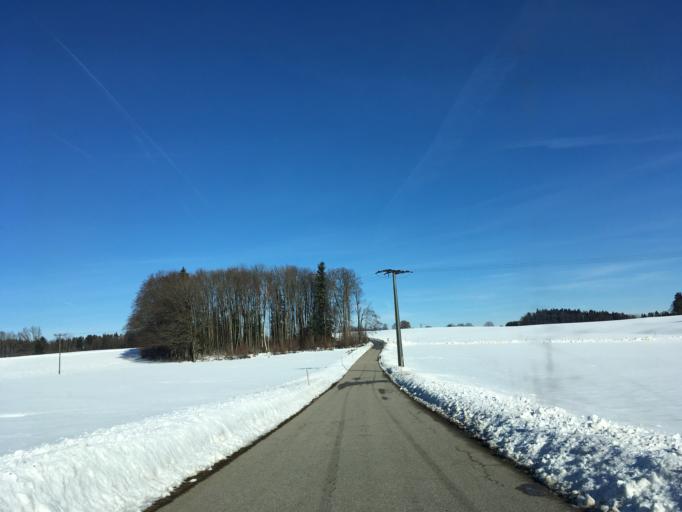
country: DE
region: Bavaria
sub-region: Upper Bavaria
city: Aschau im Chiemgau
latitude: 47.8103
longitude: 12.3366
